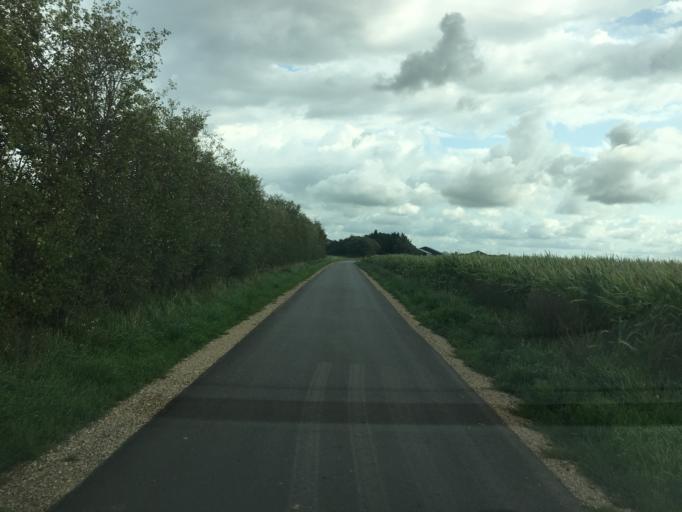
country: DK
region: South Denmark
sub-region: Tonder Kommune
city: Tonder
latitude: 54.9521
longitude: 8.8993
